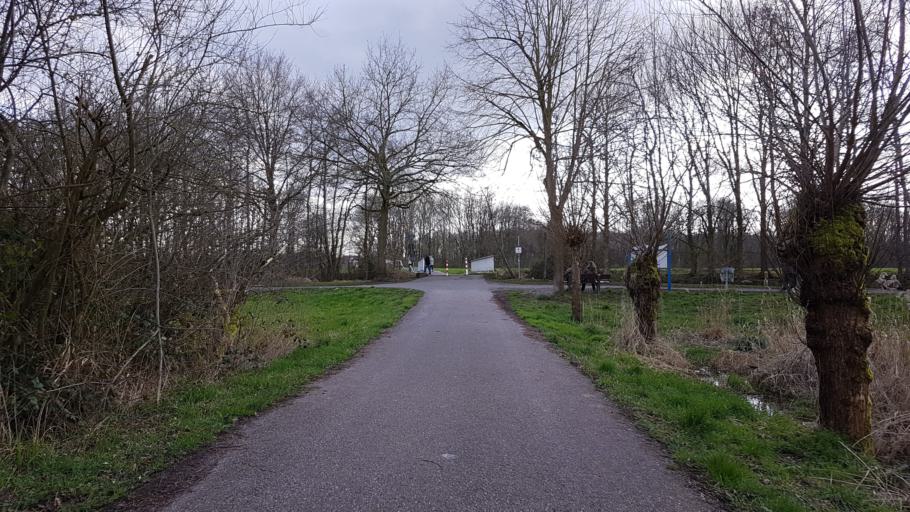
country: DE
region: North Rhine-Westphalia
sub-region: Regierungsbezirk Dusseldorf
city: Bruggen
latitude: 51.2390
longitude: 6.2090
